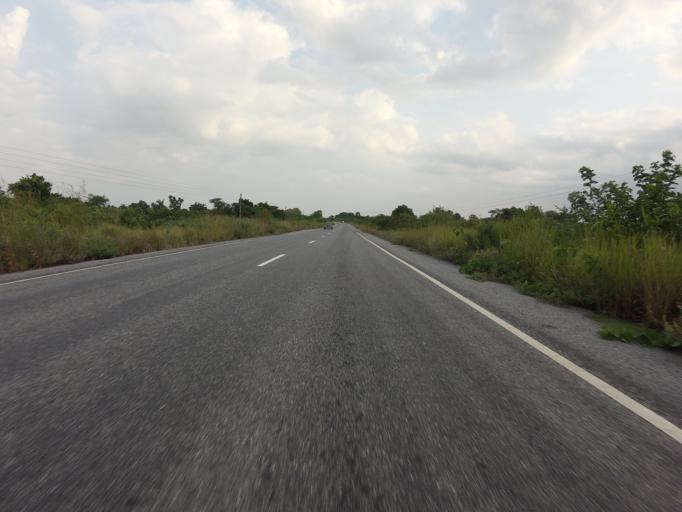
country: GH
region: Volta
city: Ho
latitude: 6.3566
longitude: 0.5367
